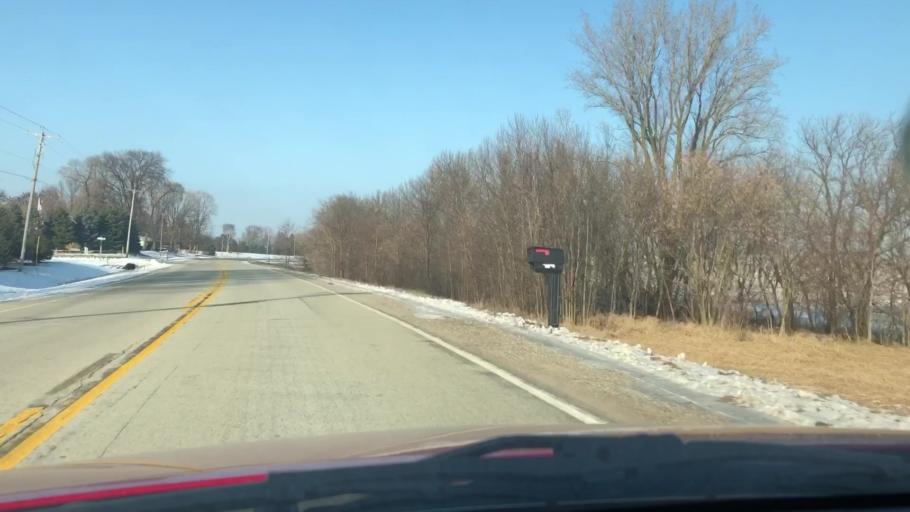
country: US
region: Wisconsin
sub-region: Outagamie County
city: Black Creek
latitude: 44.3935
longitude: -88.3746
